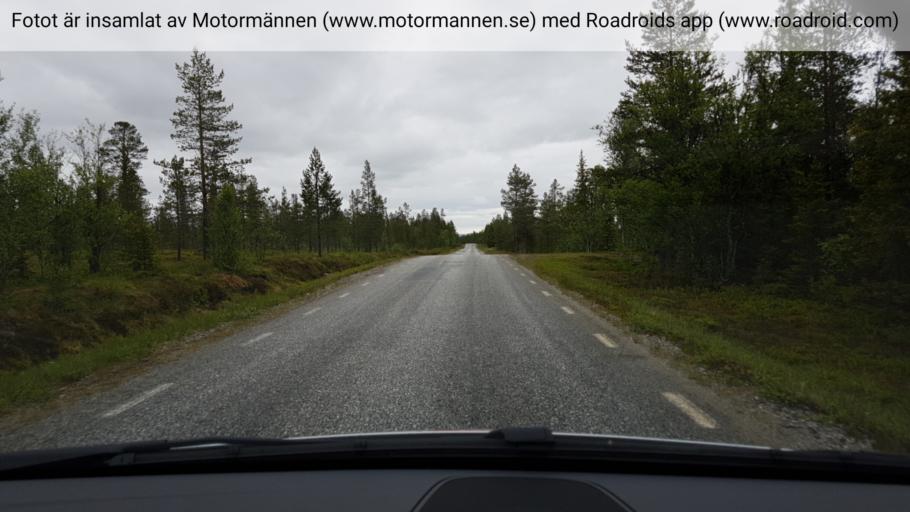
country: SE
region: Jaemtland
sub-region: Harjedalens Kommun
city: Sveg
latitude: 62.3291
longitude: 13.4225
